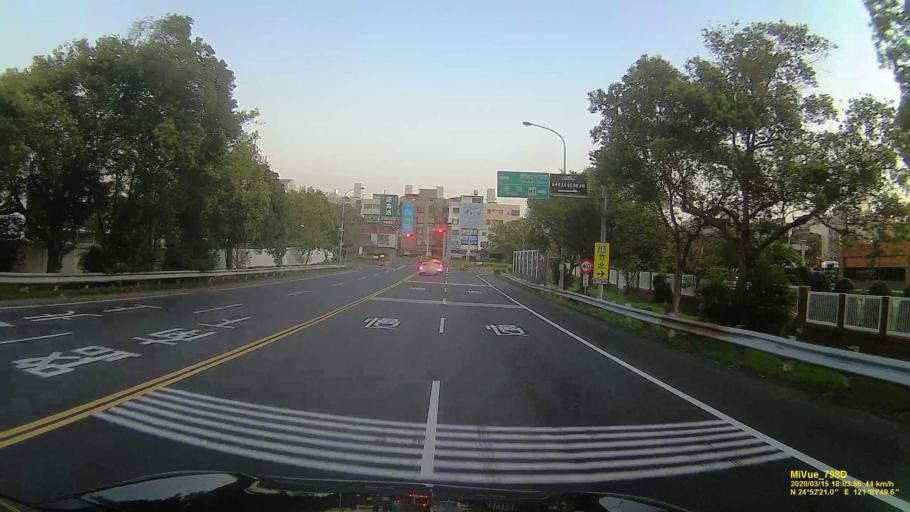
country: TW
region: Taiwan
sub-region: Hsinchu
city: Zhubei
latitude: 24.8723
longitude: 121.0305
